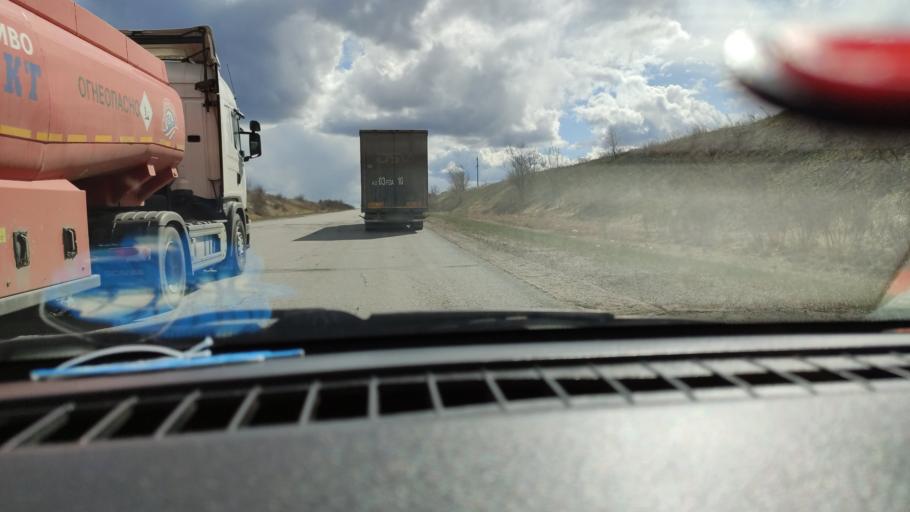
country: RU
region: Samara
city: Varlamovo
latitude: 53.0900
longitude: 48.3552
